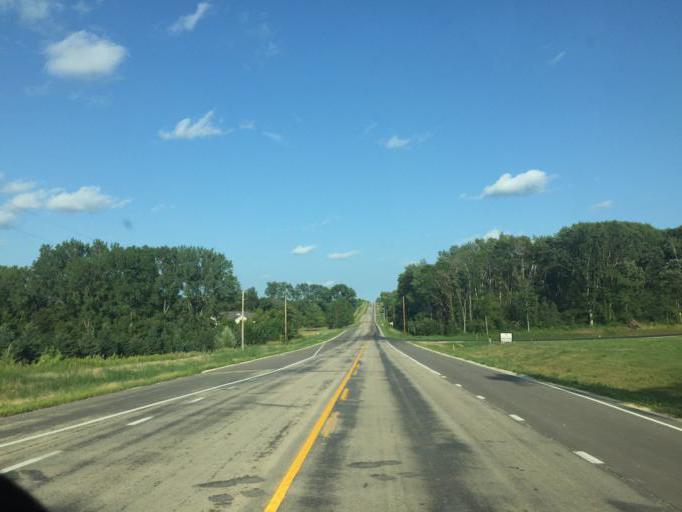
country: US
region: Minnesota
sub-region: Olmsted County
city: Rochester
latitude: 43.9640
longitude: -92.5433
